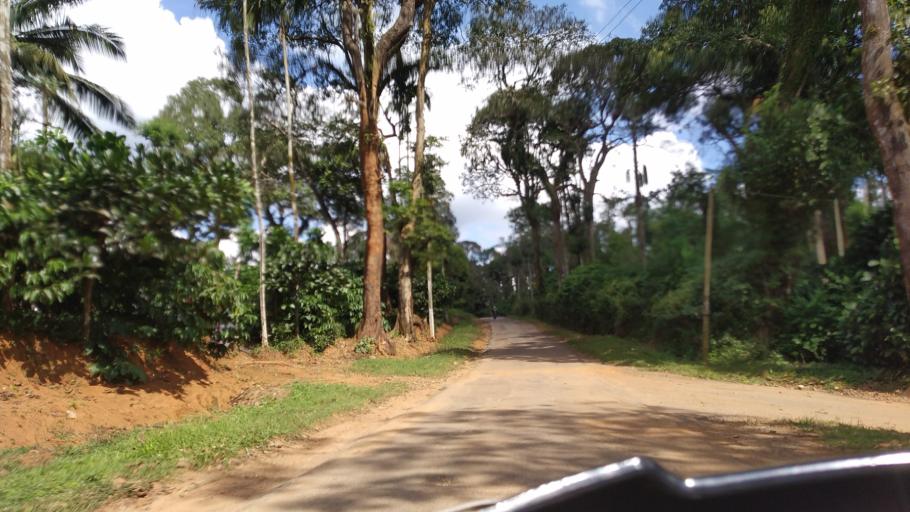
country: IN
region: Karnataka
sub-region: Kodagu
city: Ponnampet
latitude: 12.0349
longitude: 75.9036
